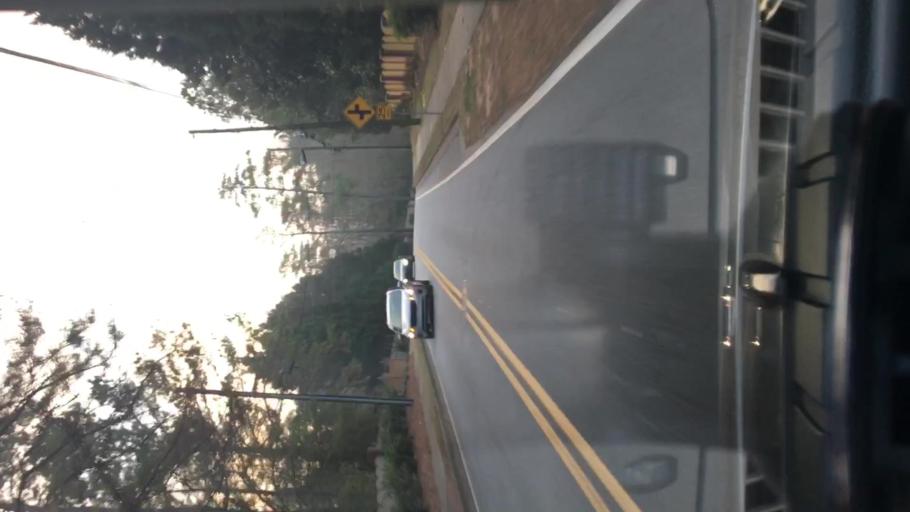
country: US
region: Georgia
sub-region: DeKalb County
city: North Atlanta
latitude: 33.8915
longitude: -84.3614
